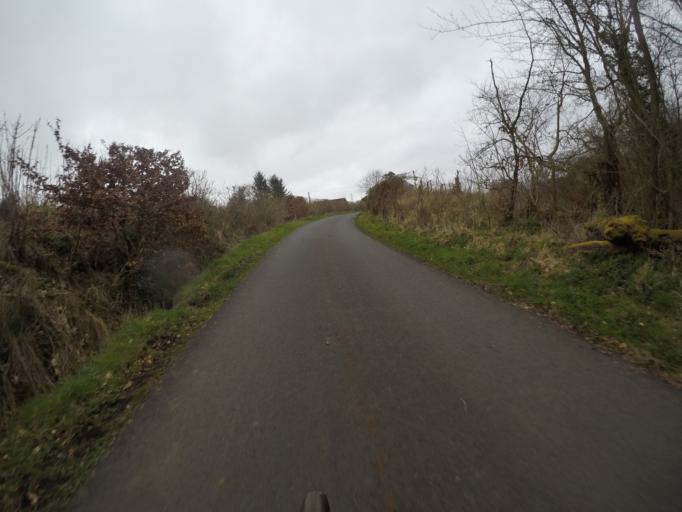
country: GB
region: Scotland
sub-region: East Ayrshire
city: Newmilns
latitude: 55.6146
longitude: -4.3535
